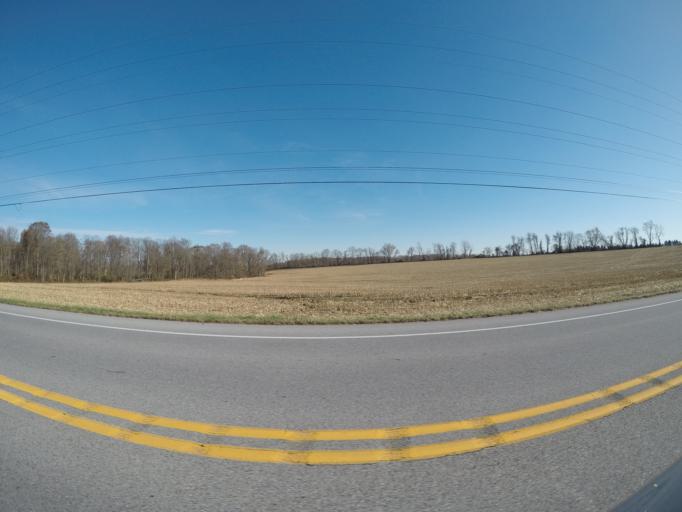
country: US
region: Pennsylvania
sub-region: Chester County
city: Parkesburg
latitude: 39.9272
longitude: -75.9158
